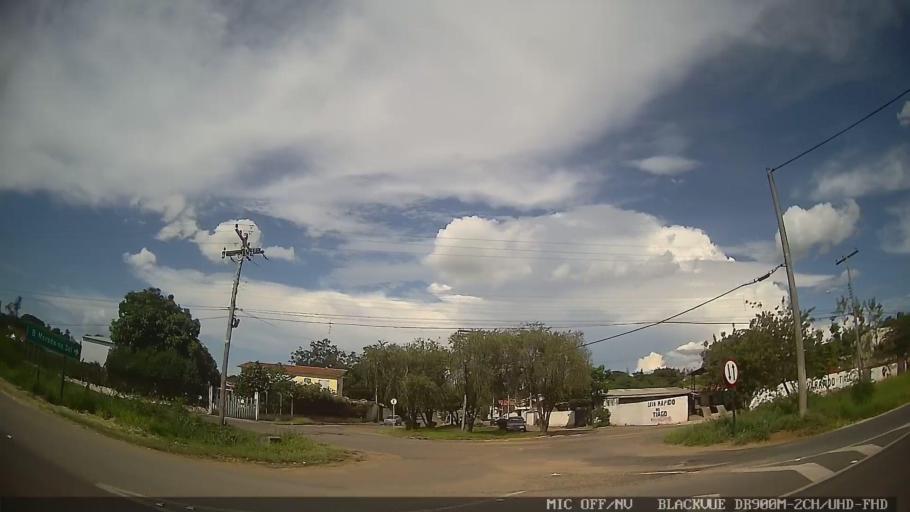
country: BR
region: Sao Paulo
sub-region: Conchas
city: Conchas
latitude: -23.0695
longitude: -47.9734
